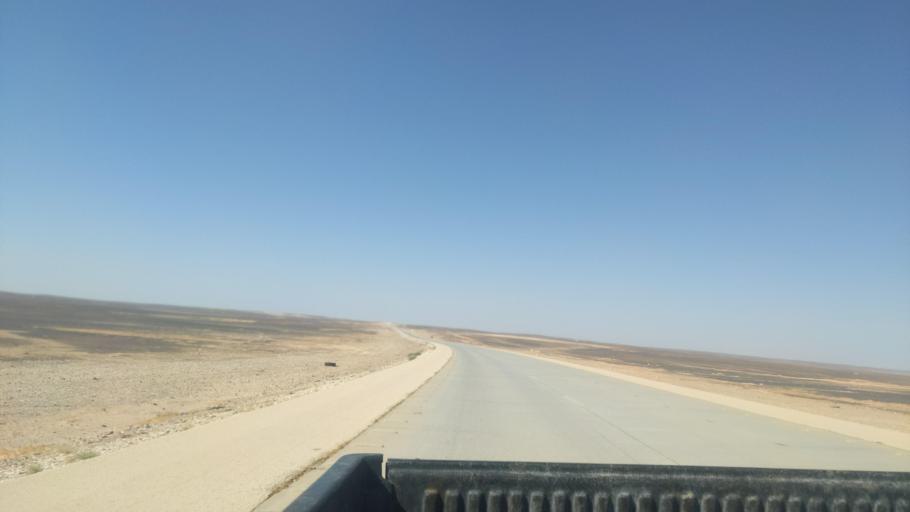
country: JO
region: Amman
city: Al Azraq ash Shamali
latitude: 31.4230
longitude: 36.7261
